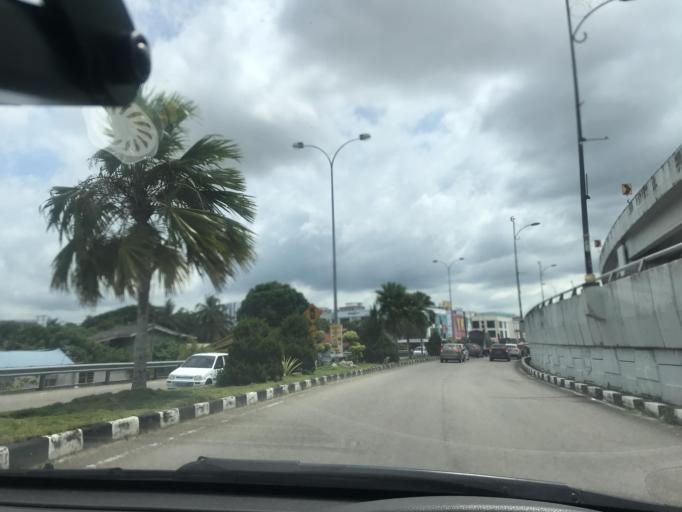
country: MY
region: Kelantan
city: Kota Bharu
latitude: 6.1152
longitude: 102.2352
